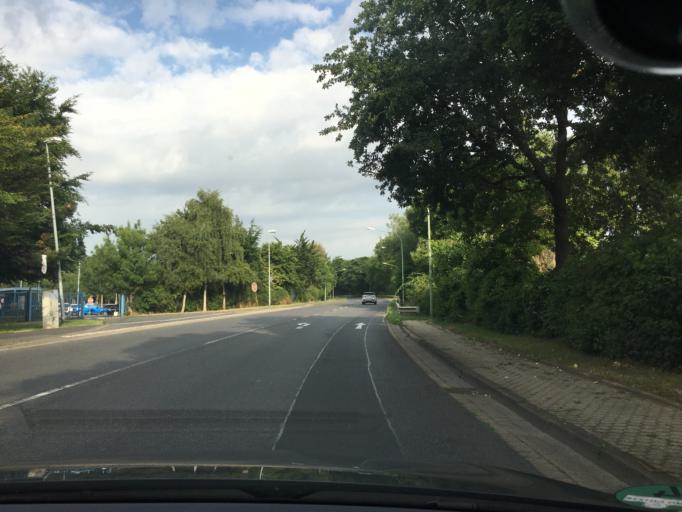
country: DE
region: North Rhine-Westphalia
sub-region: Regierungsbezirk Koln
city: Dueren
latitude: 50.8286
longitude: 6.4540
